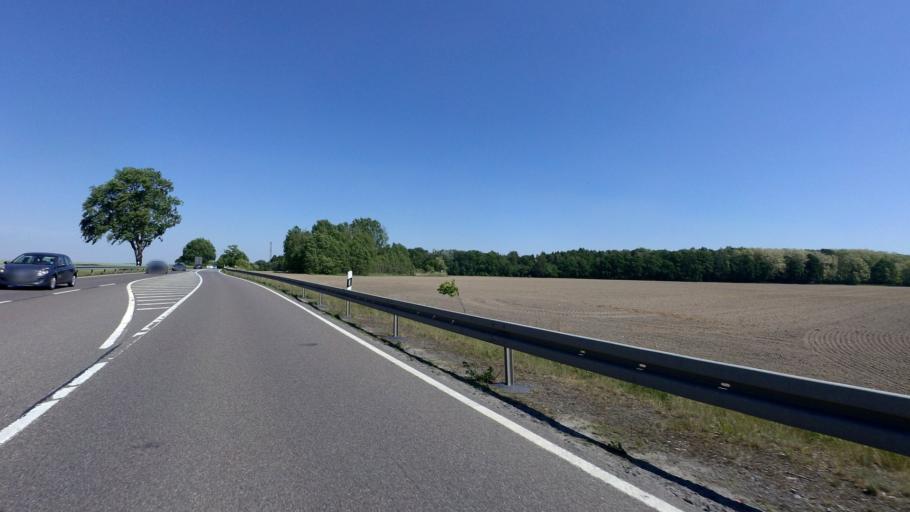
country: DE
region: Brandenburg
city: Spremberg
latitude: 51.6521
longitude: 14.3612
